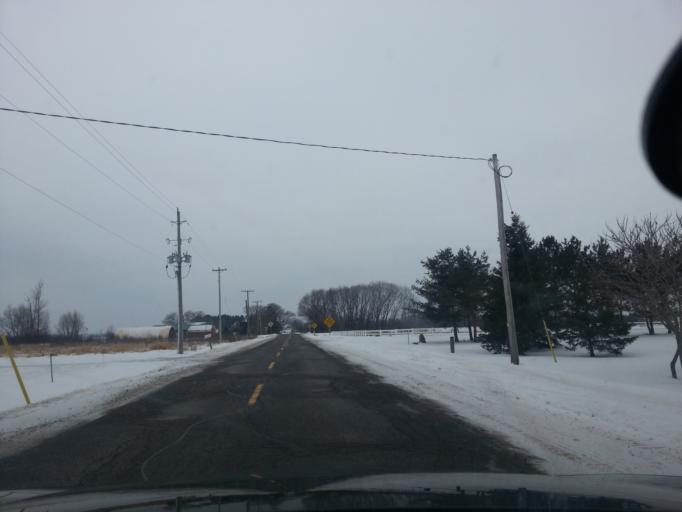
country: CA
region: Ontario
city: Bells Corners
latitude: 45.3504
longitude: -76.0568
